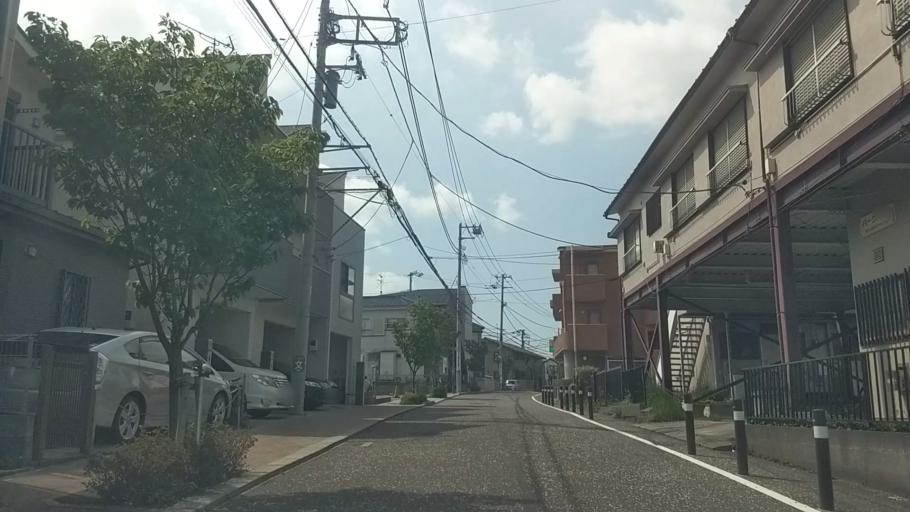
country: JP
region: Kanagawa
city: Yokohama
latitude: 35.3946
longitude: 139.5921
